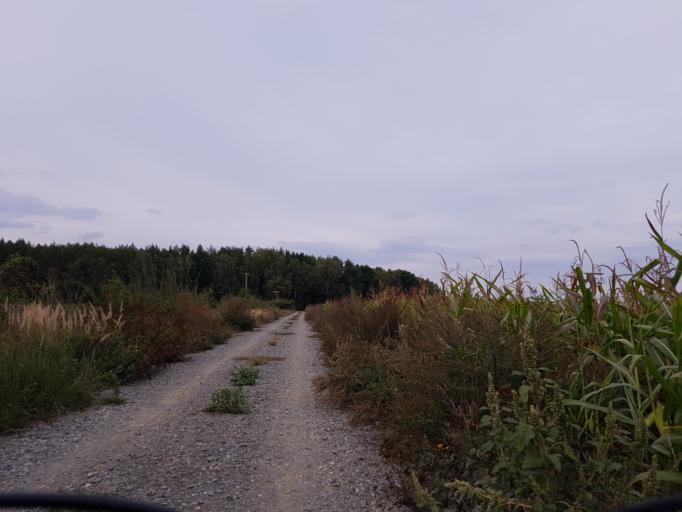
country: DE
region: Brandenburg
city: Trobitz
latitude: 51.5502
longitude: 13.4479
